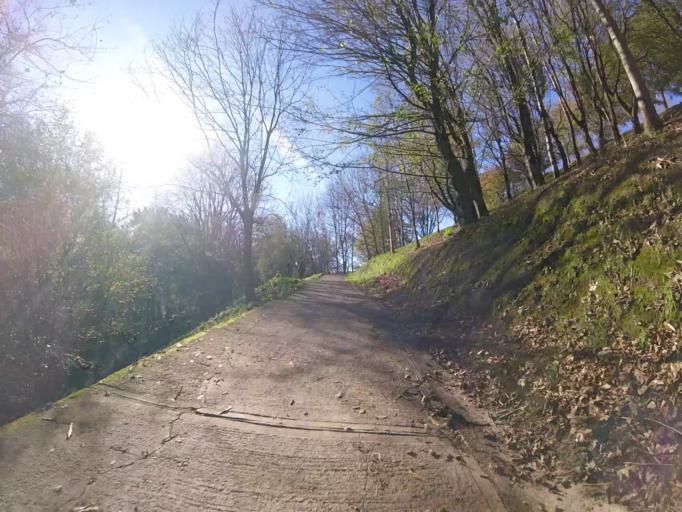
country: ES
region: Basque Country
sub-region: Provincia de Guipuzcoa
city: San Sebastian
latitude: 43.2947
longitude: -1.9891
